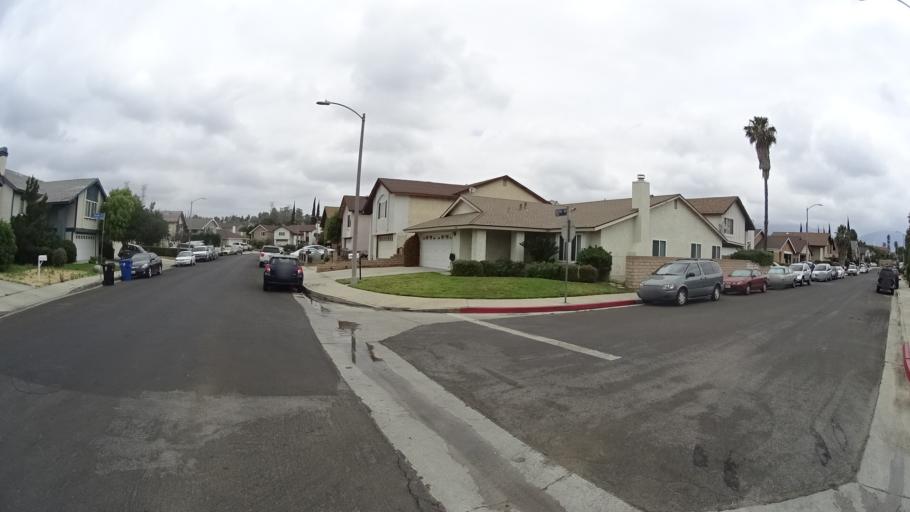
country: US
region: California
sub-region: Los Angeles County
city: San Fernando
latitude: 34.2773
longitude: -118.4590
